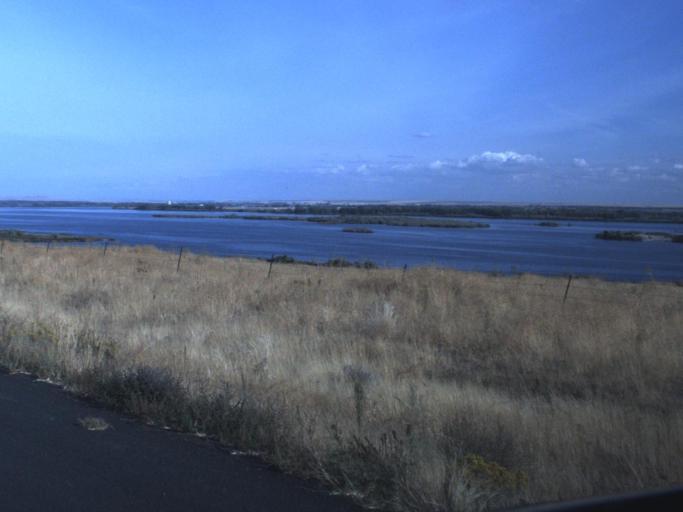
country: US
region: Oregon
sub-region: Morrow County
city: Boardman
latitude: 45.9180
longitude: -119.6510
